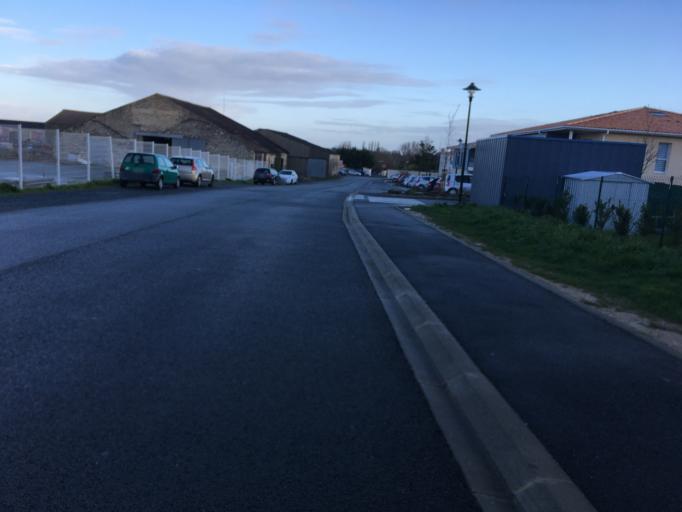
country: FR
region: Poitou-Charentes
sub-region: Departement de la Charente-Maritime
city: Nieul-sur-Mer
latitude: 46.2020
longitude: -1.1661
